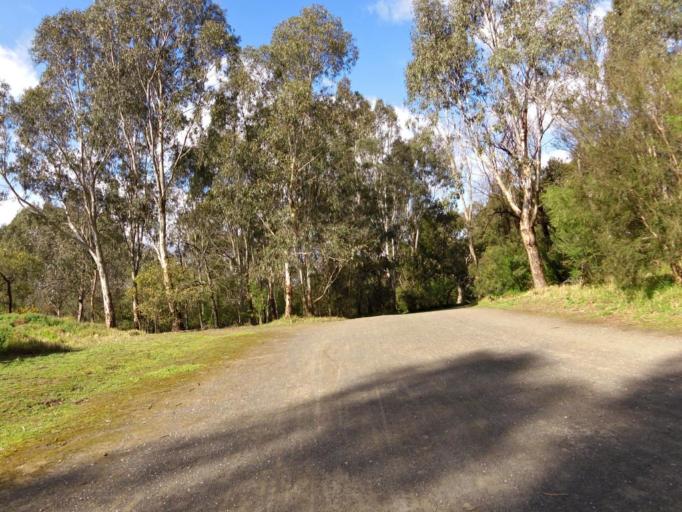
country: AU
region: Victoria
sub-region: Banyule
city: Viewbank
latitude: -37.7485
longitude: 145.0974
